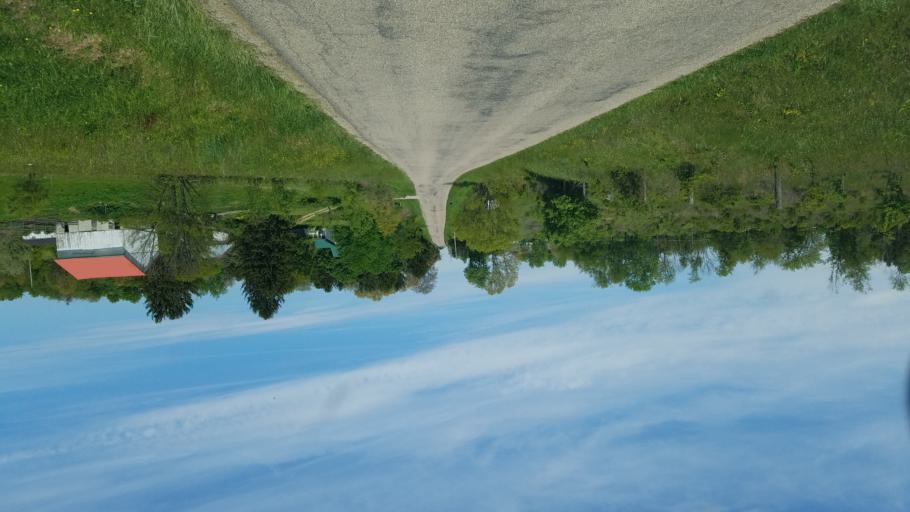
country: US
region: Ohio
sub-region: Knox County
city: Gambier
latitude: 40.3973
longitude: -82.4085
